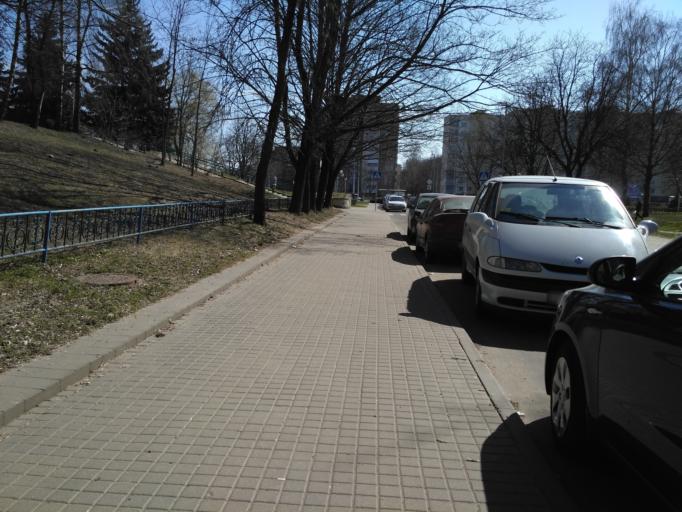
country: BY
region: Minsk
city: Novoye Medvezhino
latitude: 53.9112
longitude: 27.4990
